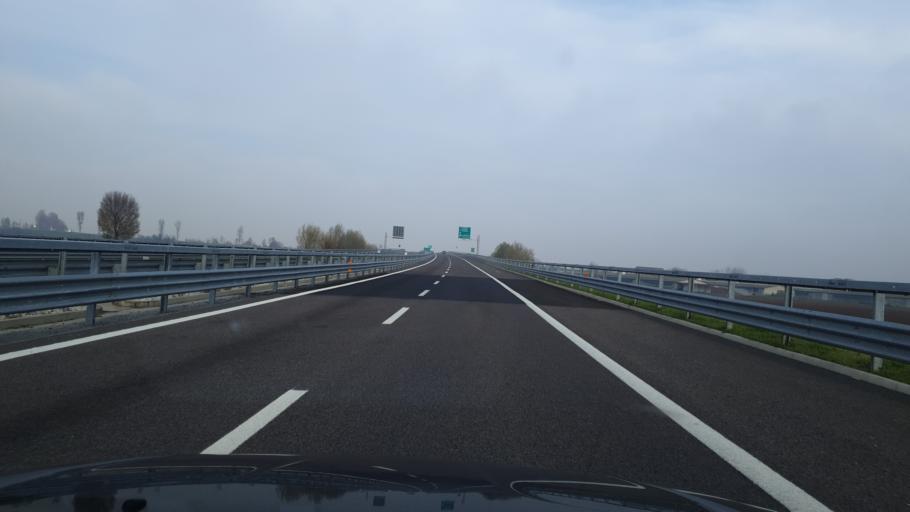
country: IT
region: Veneto
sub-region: Provincia di Padova
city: Saletto
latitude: 45.2549
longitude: 11.5694
